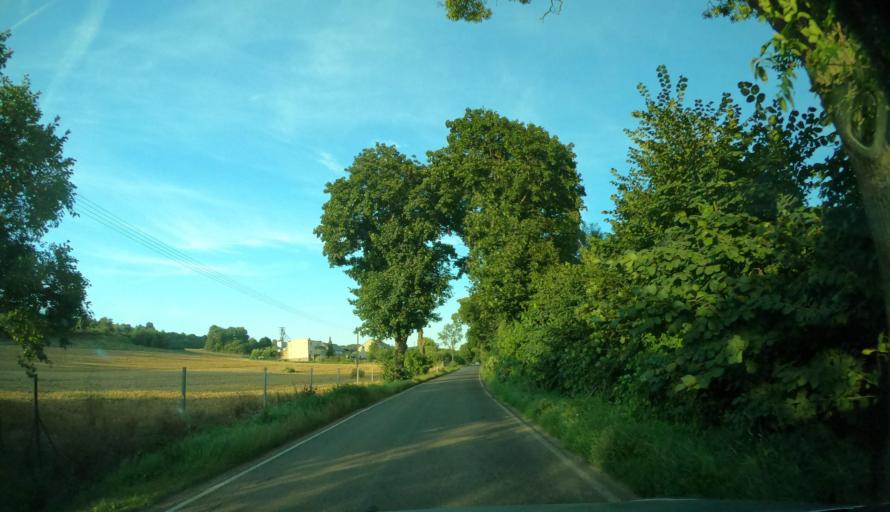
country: PL
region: Kujawsko-Pomorskie
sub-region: Bydgoszcz
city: Fordon
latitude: 53.2287
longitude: 18.2026
